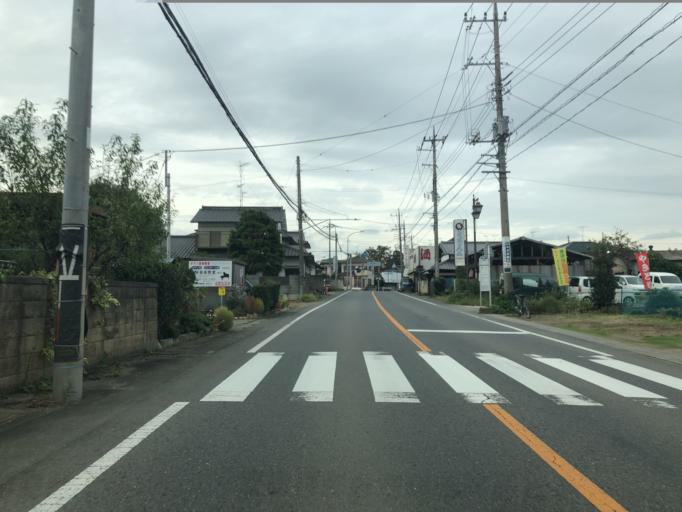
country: JP
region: Saitama
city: Fukiage-fujimi
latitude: 36.0586
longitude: 139.4073
